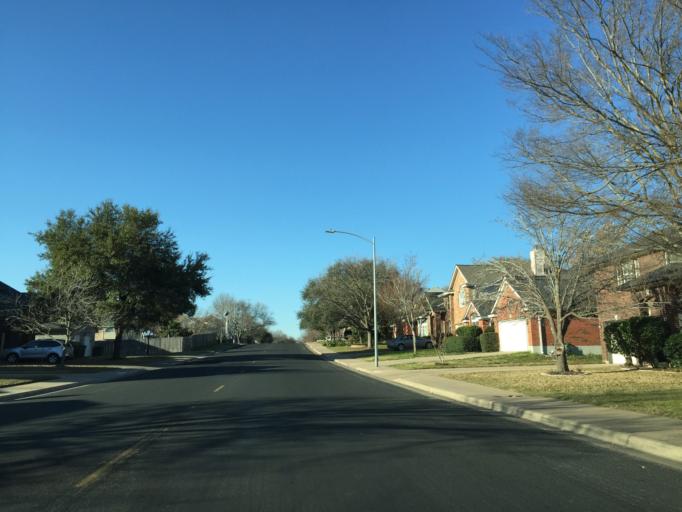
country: US
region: Texas
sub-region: Williamson County
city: Jollyville
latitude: 30.4455
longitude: -97.7661
